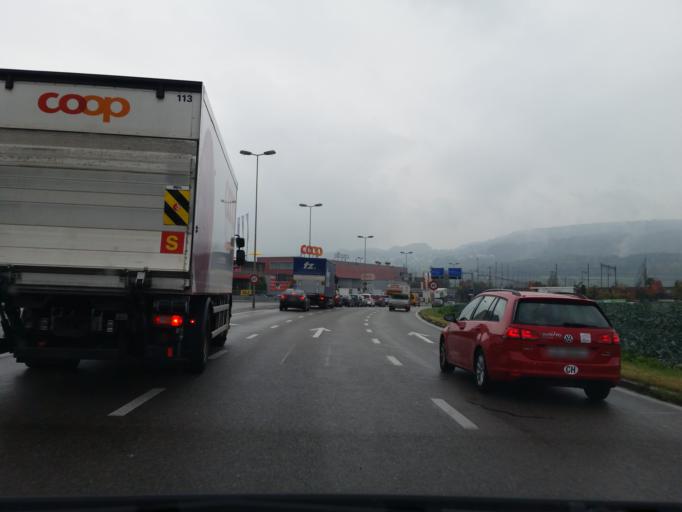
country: CH
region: Zurich
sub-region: Bezirk Dietikon
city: Dietikon / Vorstadt
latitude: 47.4210
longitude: 8.3923
